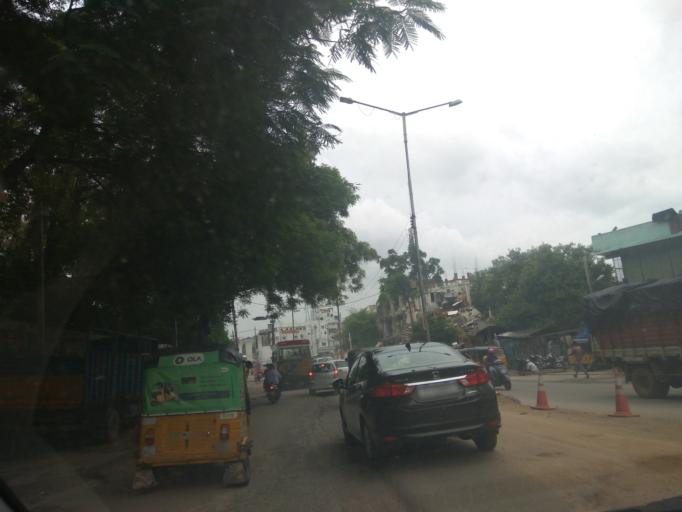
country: IN
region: Telangana
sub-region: Hyderabad
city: Malkajgiri
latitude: 17.4214
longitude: 78.5012
